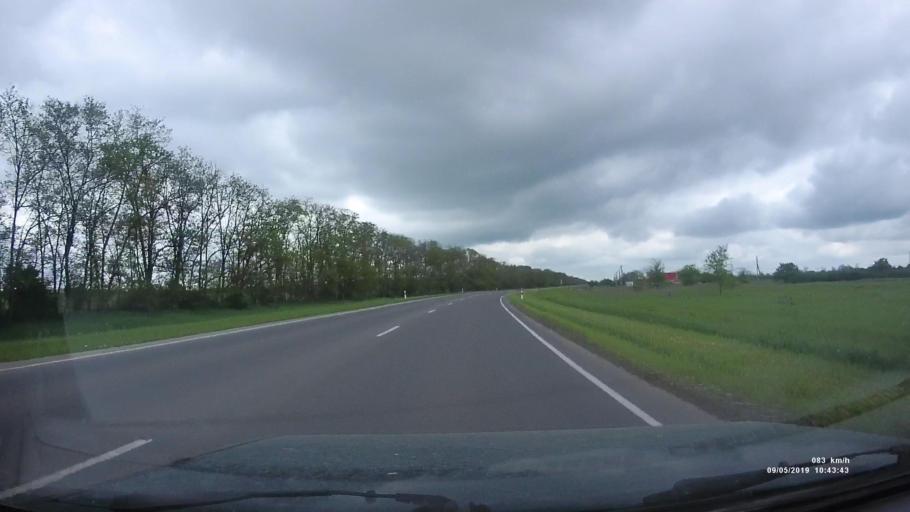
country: RU
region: Rostov
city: Peshkovo
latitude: 47.0053
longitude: 39.4006
